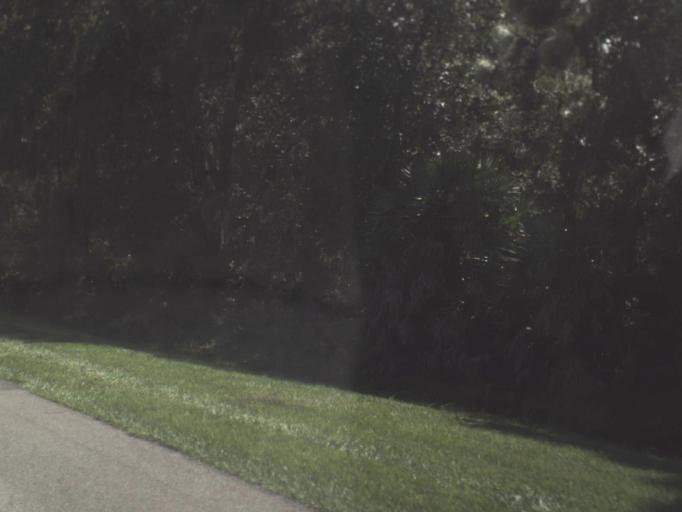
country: US
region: Florida
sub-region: Sarasota County
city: The Meadows
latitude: 27.4114
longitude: -82.3397
